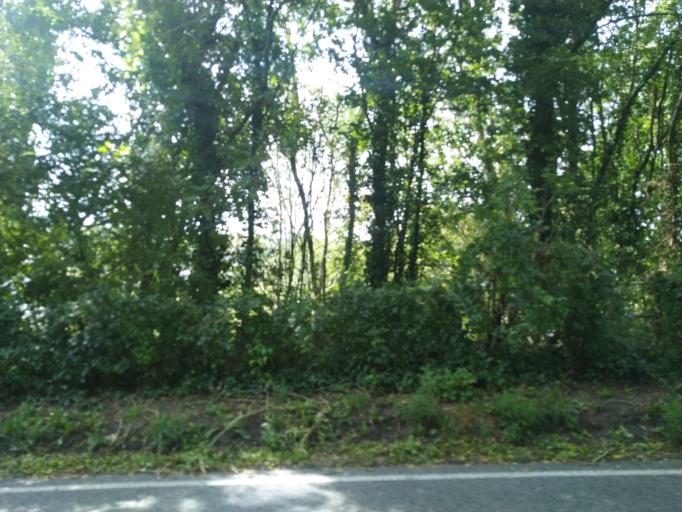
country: GB
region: England
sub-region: Dorset
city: Blandford Forum
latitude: 50.8774
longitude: -2.1953
